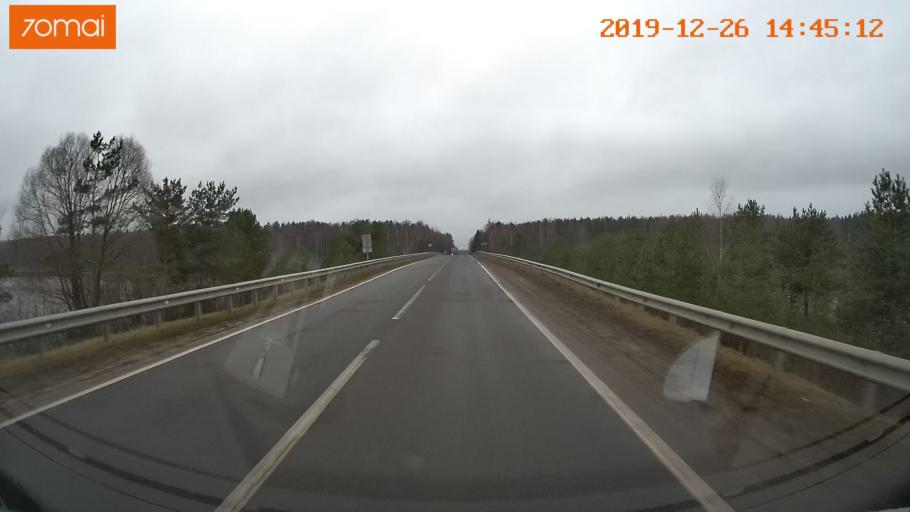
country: RU
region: Jaroslavl
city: Poshekhon'ye
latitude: 58.3396
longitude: 39.0448
